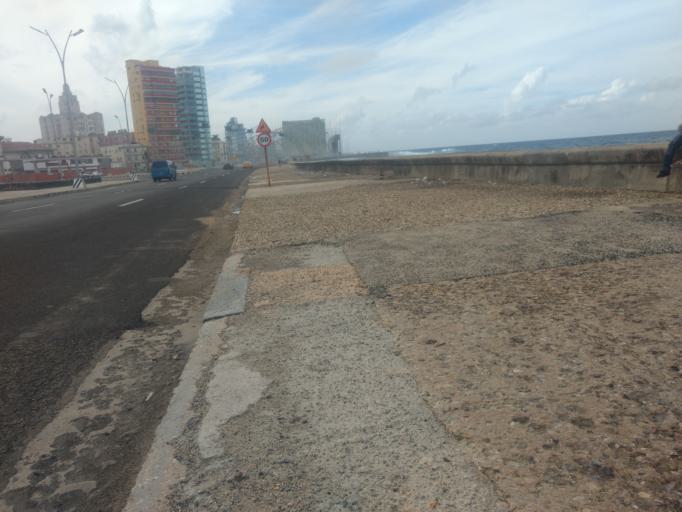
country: CU
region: La Habana
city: Havana
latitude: 23.1453
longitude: -82.3828
